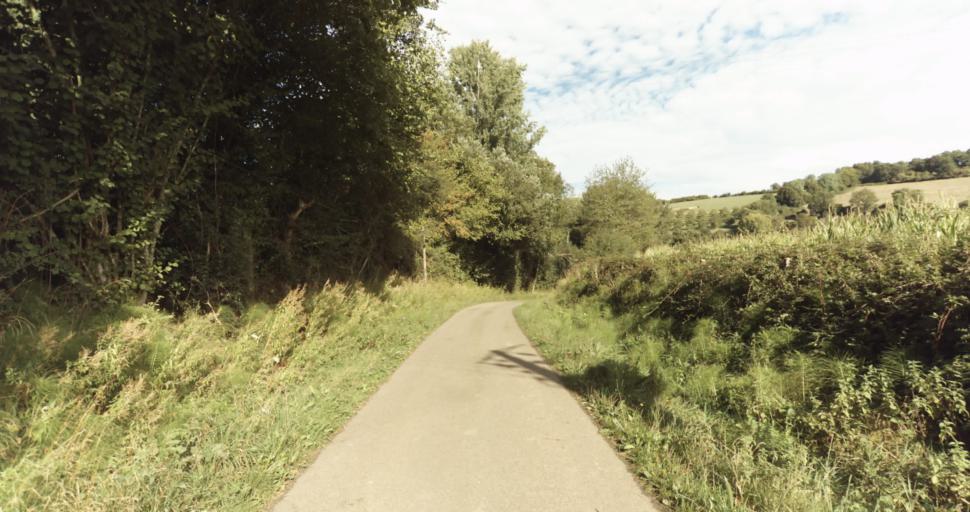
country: FR
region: Lower Normandy
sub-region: Departement de l'Orne
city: Gace
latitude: 48.8124
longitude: 0.2153
